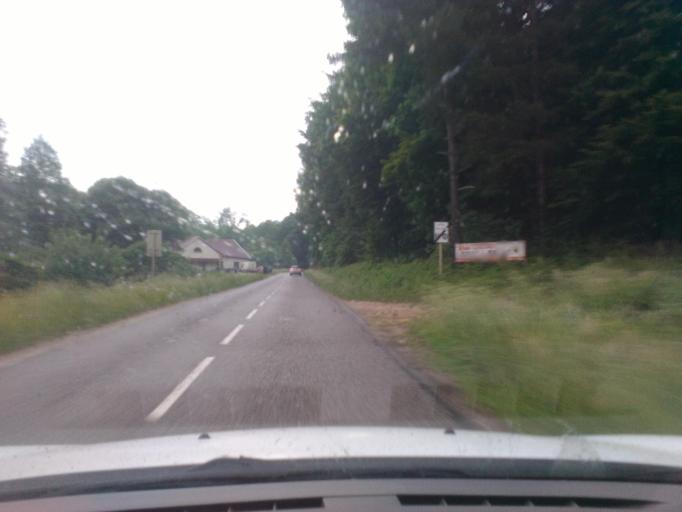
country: FR
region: Lorraine
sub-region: Departement des Vosges
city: Bruyeres
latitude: 48.2742
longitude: 6.7160
